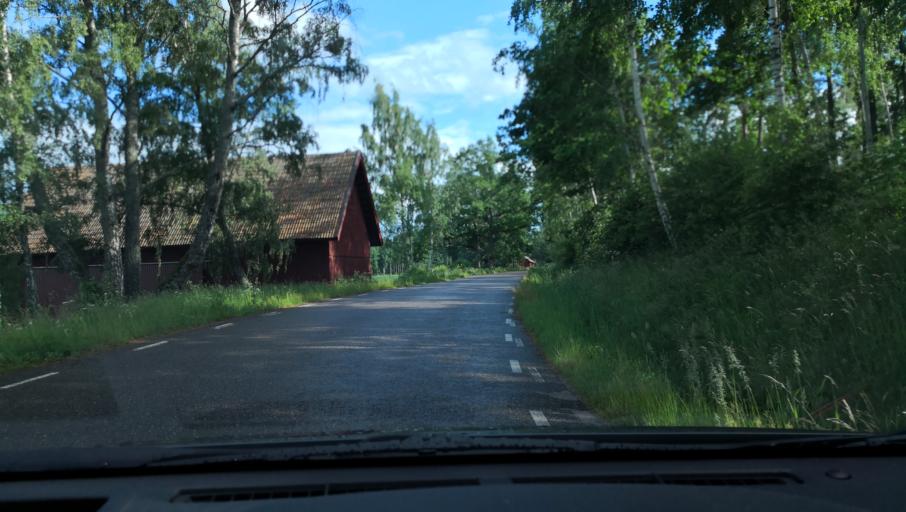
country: SE
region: OErebro
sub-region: Lindesbergs Kommun
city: Fellingsbro
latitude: 59.3082
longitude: 15.6803
